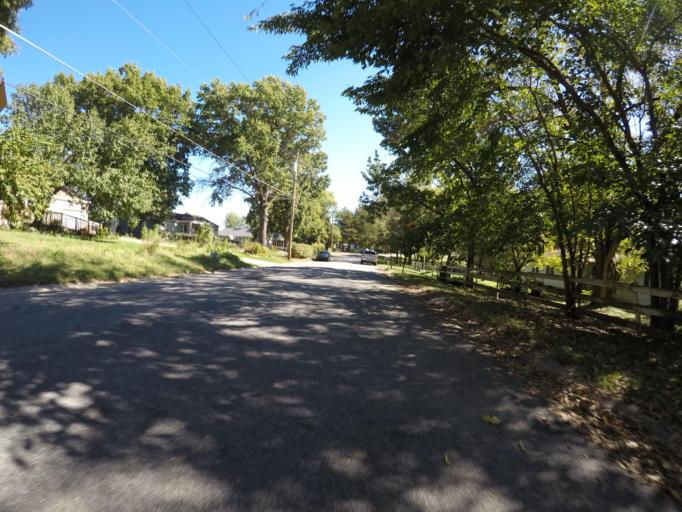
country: US
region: Kansas
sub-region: Wyandotte County
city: Bonner Springs
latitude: 39.0562
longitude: -94.8930
